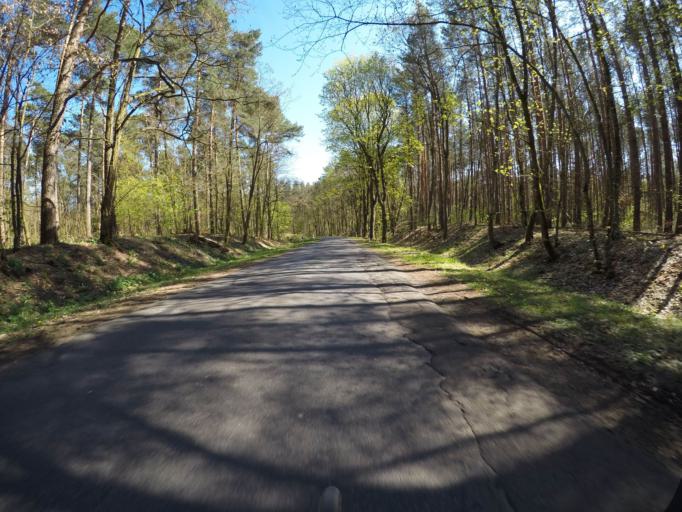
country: DE
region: Brandenburg
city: Werftpfuhl
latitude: 52.6188
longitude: 13.8285
